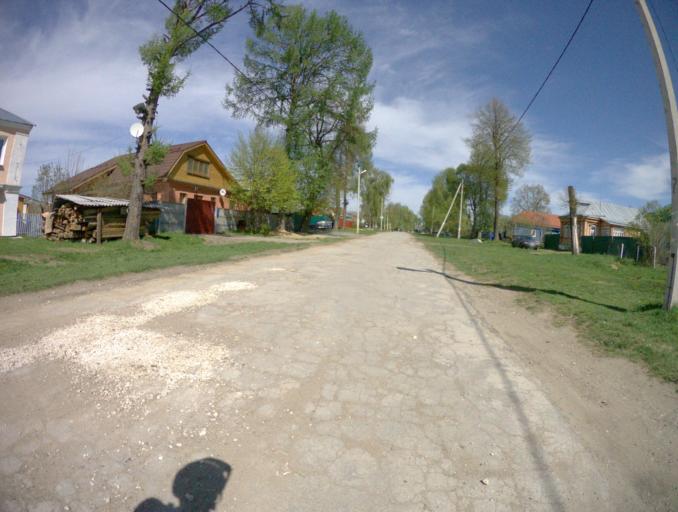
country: RU
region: Vladimir
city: Orgtrud
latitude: 56.2081
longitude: 40.5762
